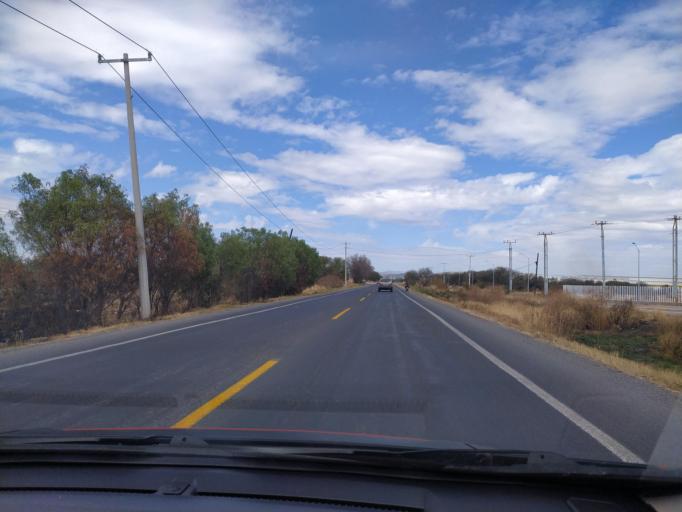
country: LA
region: Oudomxai
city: Muang La
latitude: 20.9991
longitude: 101.8327
